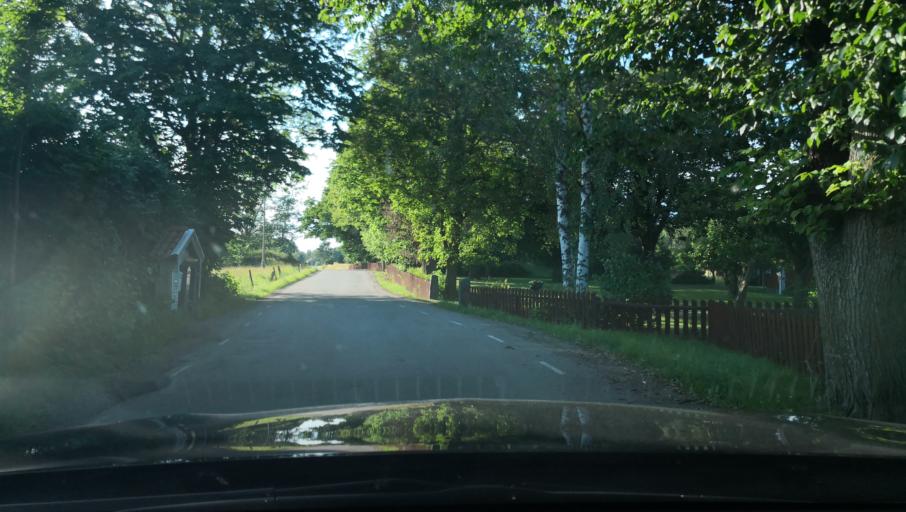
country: SE
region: Uppsala
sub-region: Uppsala Kommun
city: Vattholma
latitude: 59.9270
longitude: 17.8376
